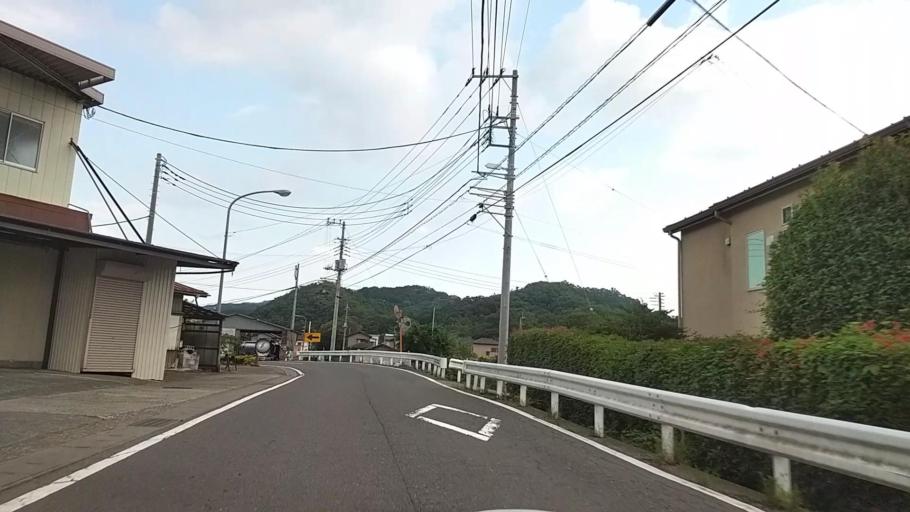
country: JP
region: Yamanashi
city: Uenohara
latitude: 35.6169
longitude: 139.1285
